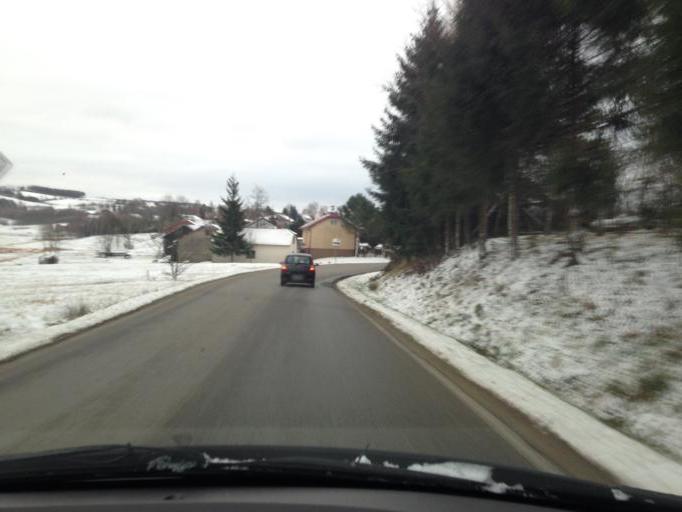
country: PL
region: Lesser Poland Voivodeship
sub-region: Powiat gorlicki
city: Moszczenica
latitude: 49.7409
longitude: 21.0849
